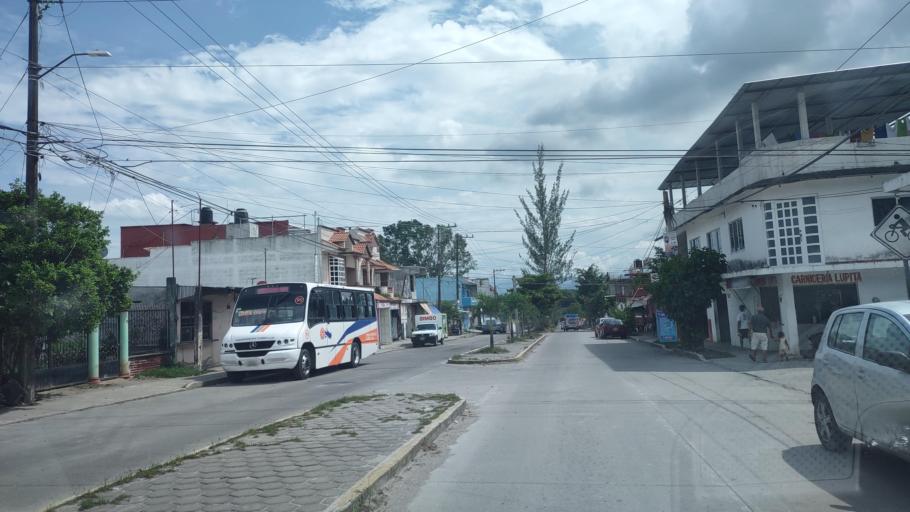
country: MX
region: Veracruz
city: Martinez de la Torre
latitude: 20.0733
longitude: -97.0764
